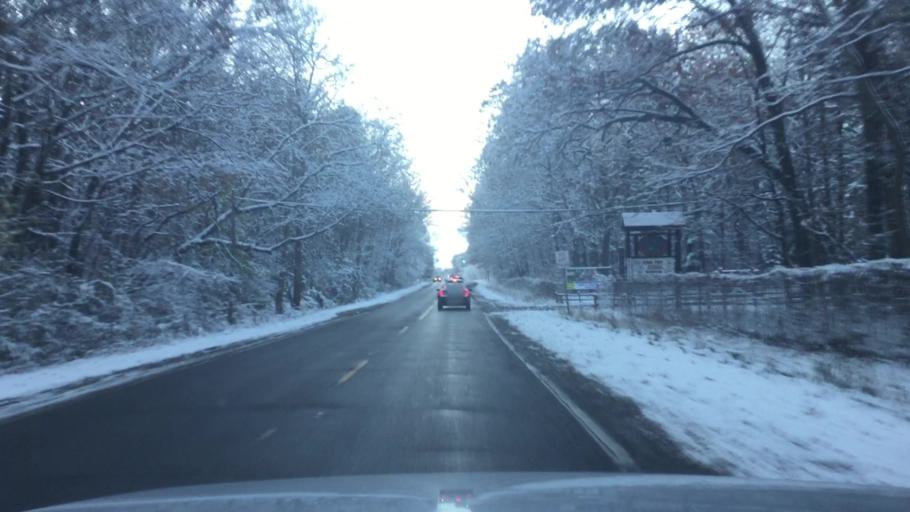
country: US
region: Michigan
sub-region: Oakland County
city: Wolverine Lake
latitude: 42.5794
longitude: -83.4705
